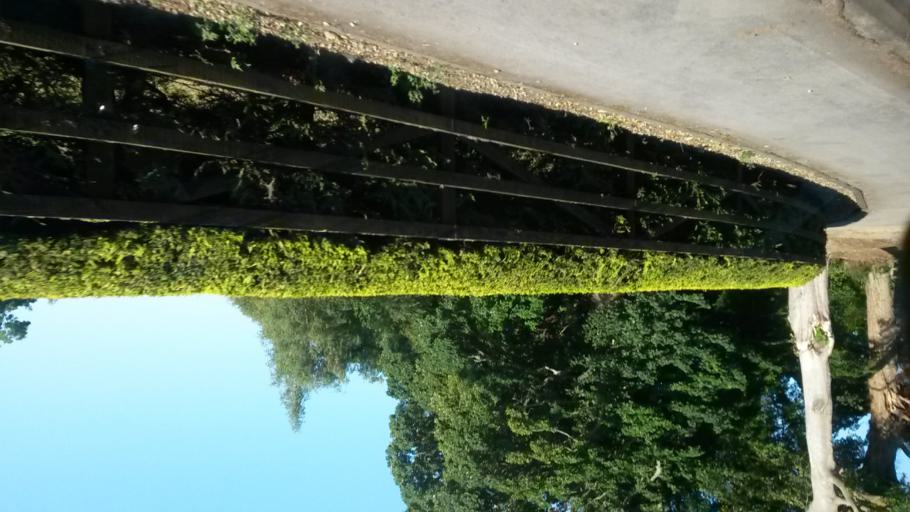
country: IE
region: Leinster
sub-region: Dublin City
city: Finglas
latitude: 53.4591
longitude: -6.3227
